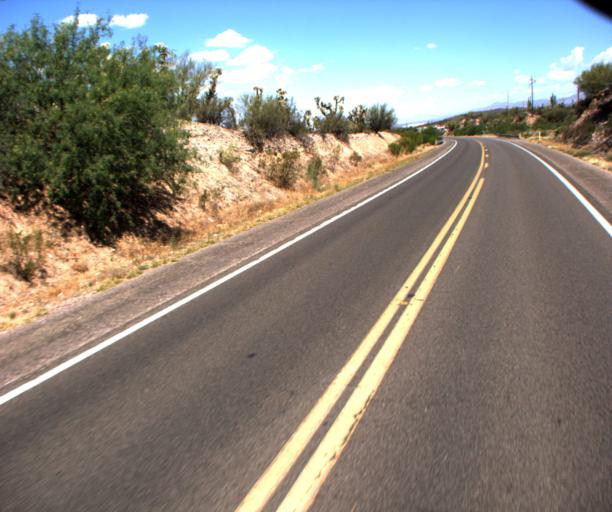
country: US
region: Arizona
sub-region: Pinal County
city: Mammoth
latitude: 32.9270
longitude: -110.7294
